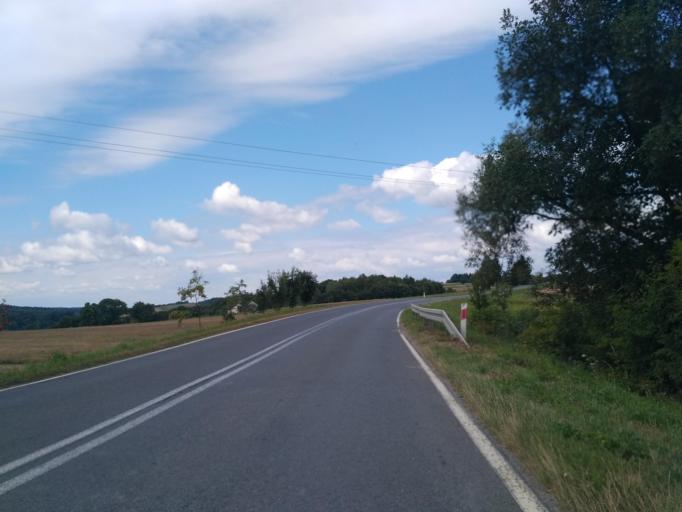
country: PL
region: Subcarpathian Voivodeship
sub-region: Powiat przeworski
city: Jawornik Polski
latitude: 49.8862
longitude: 22.2427
